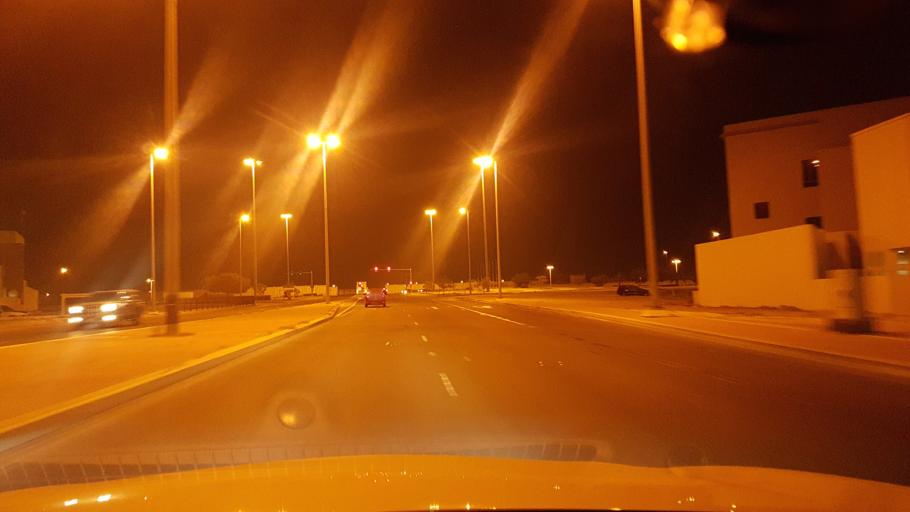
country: BH
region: Central Governorate
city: Madinat Hamad
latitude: 26.0972
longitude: 50.5088
